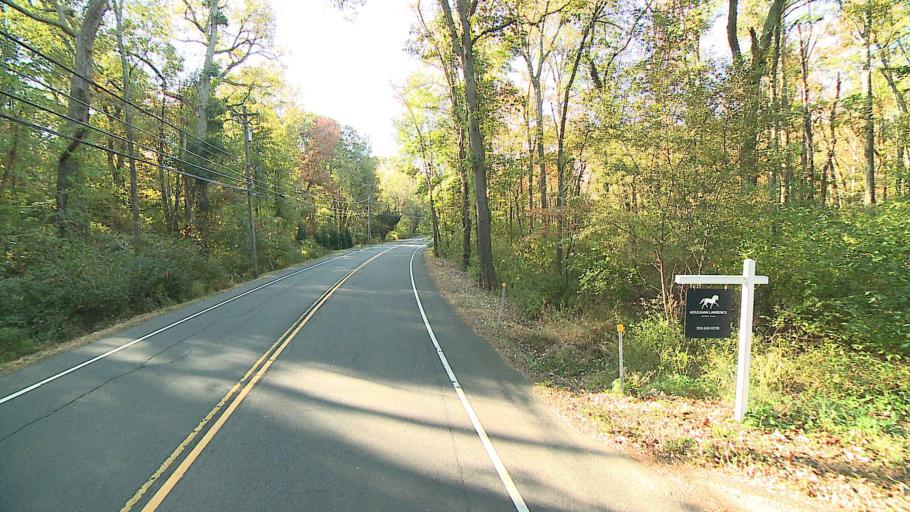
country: US
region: Connecticut
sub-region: Fairfield County
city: Wilton
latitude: 41.2201
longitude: -73.3837
